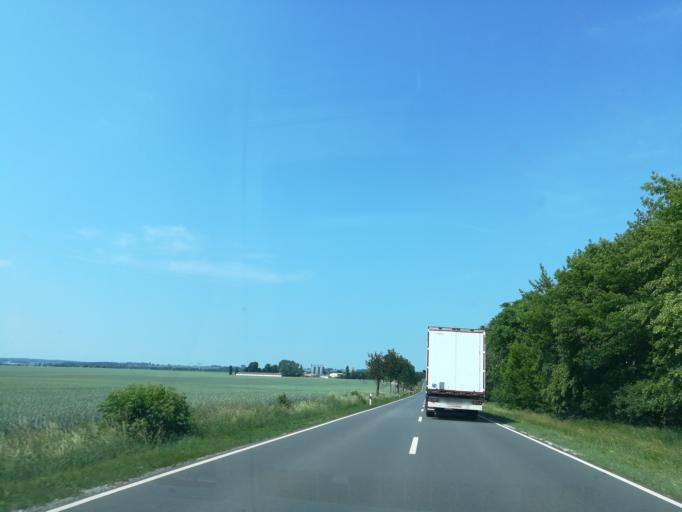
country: DE
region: Saxony-Anhalt
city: Aschersleben
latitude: 51.7898
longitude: 11.4590
